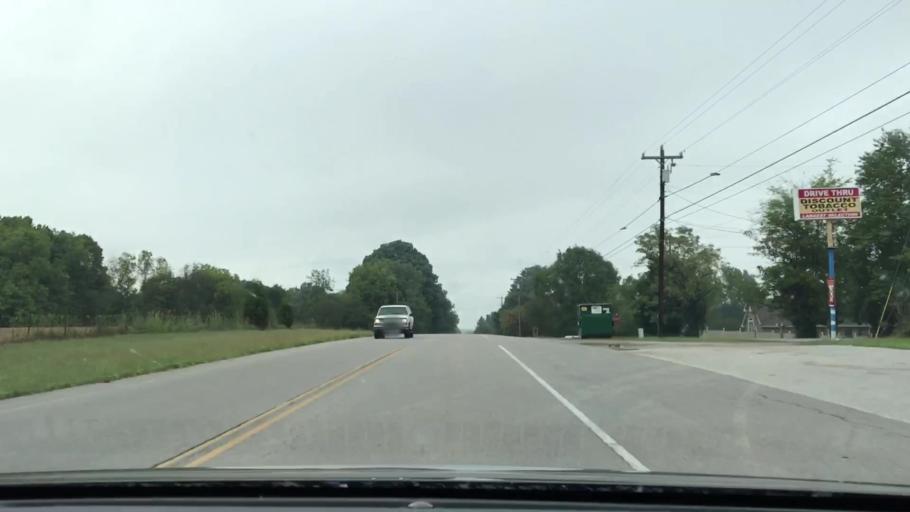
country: US
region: Tennessee
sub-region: Sumner County
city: Portland
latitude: 36.5124
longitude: -86.5000
